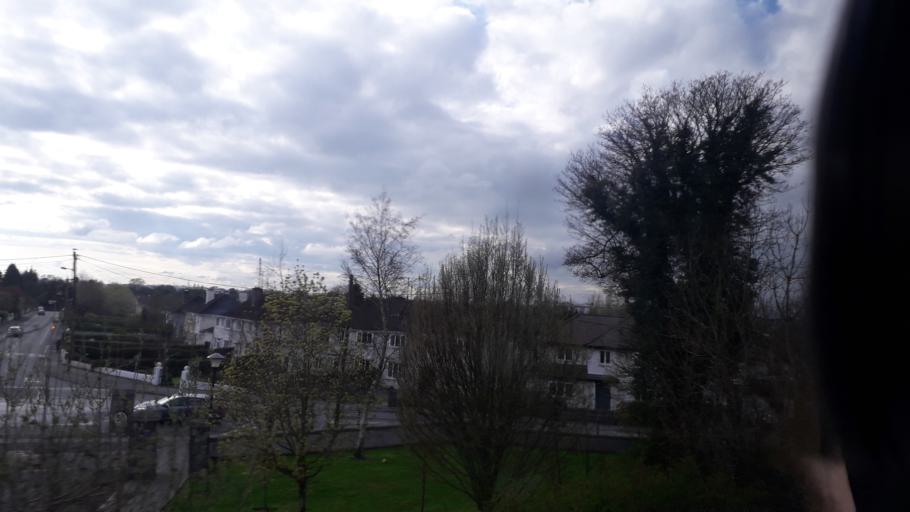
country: IE
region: Leinster
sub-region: An Iarmhi
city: An Muileann gCearr
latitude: 53.5193
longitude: -7.3338
